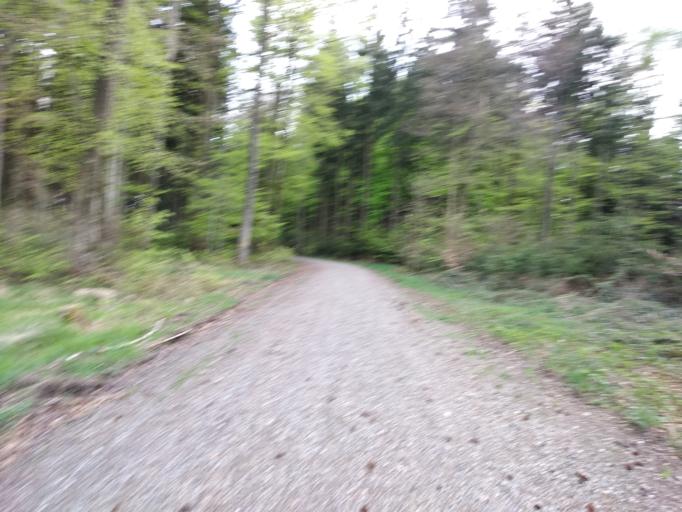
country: DE
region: Bavaria
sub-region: Swabia
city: Woringen
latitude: 47.9271
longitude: 10.1898
